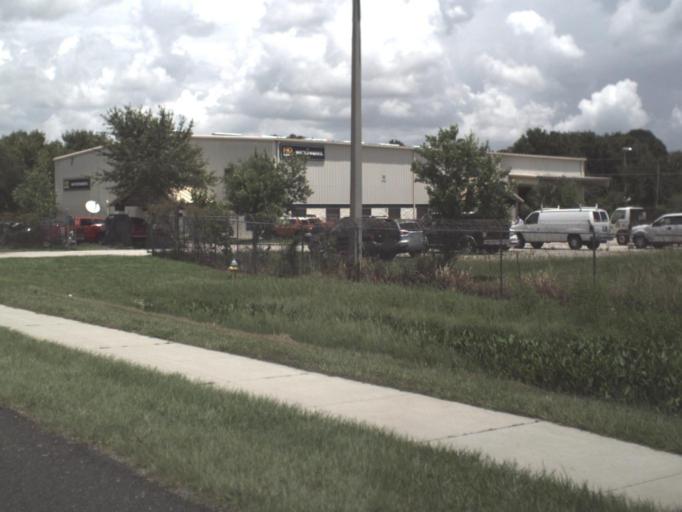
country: US
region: Florida
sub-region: Hillsborough County
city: East Lake-Orient Park
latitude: 28.0063
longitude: -82.3556
